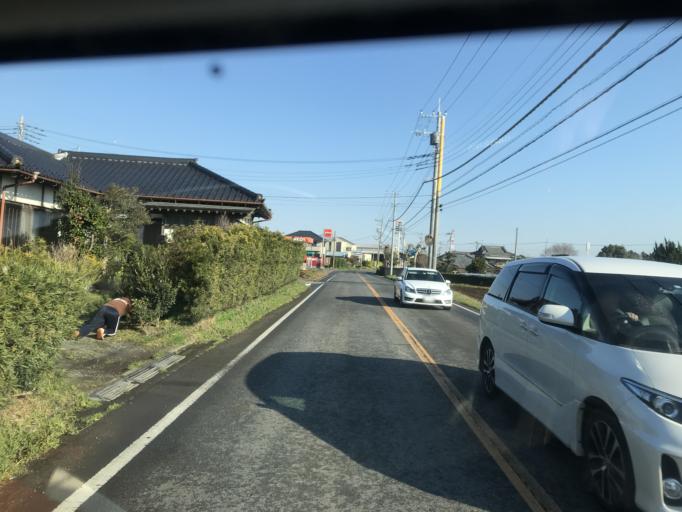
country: JP
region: Chiba
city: Sawara
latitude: 35.8511
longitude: 140.5089
